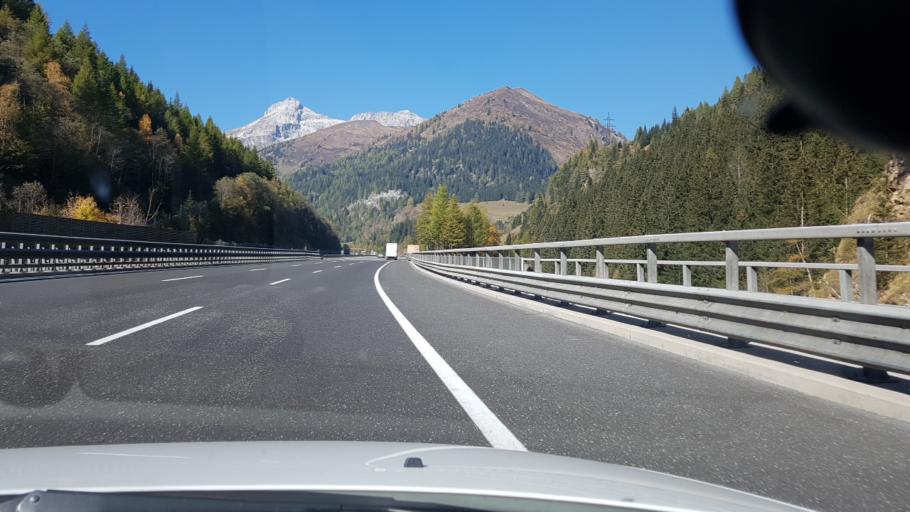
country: AT
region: Salzburg
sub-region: Politischer Bezirk Tamsweg
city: Zederhaus
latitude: 47.1742
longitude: 13.4490
